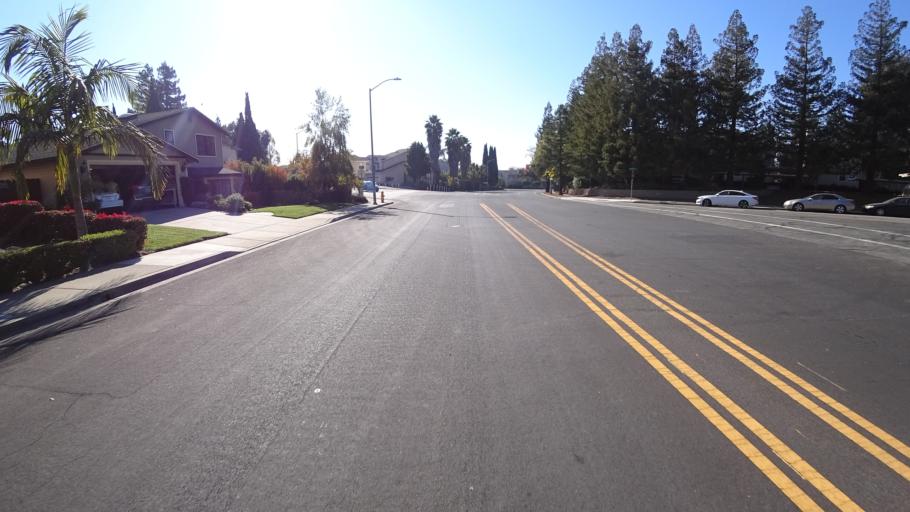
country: US
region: California
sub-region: Alameda County
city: Union City
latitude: 37.6314
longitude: -122.0448
